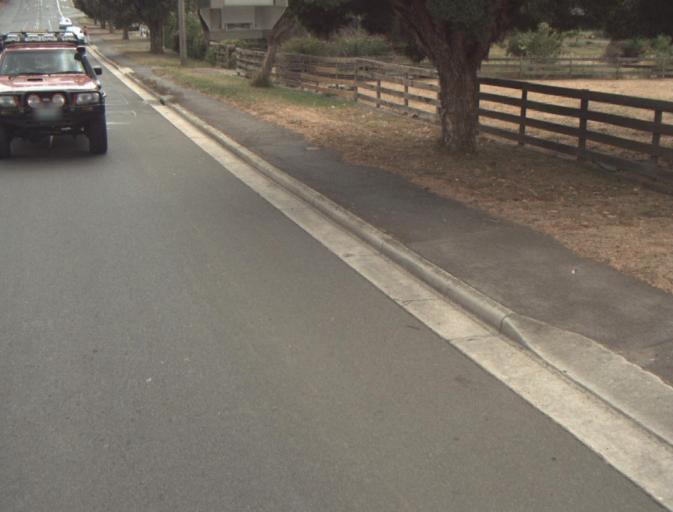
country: AU
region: Tasmania
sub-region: Launceston
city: Newstead
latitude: -41.4720
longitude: 147.1714
